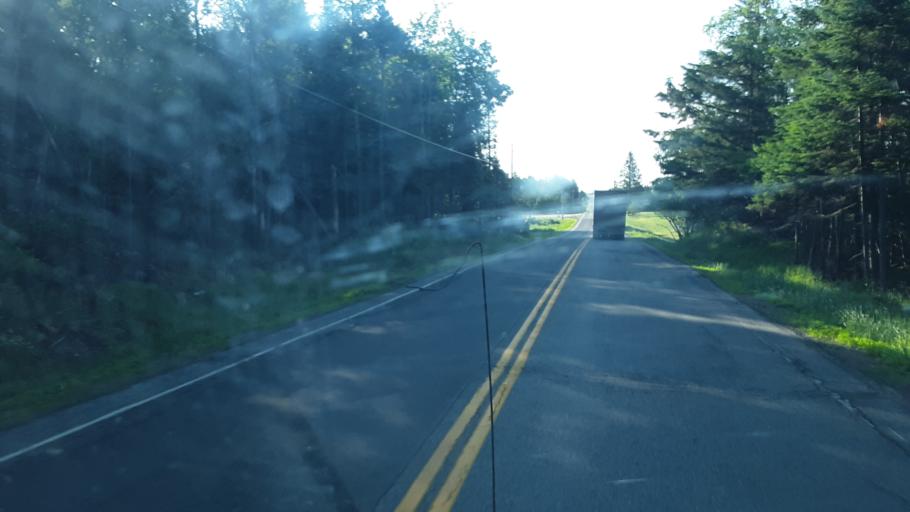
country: US
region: Maine
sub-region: Penobscot County
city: Patten
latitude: 46.1421
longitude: -68.2043
